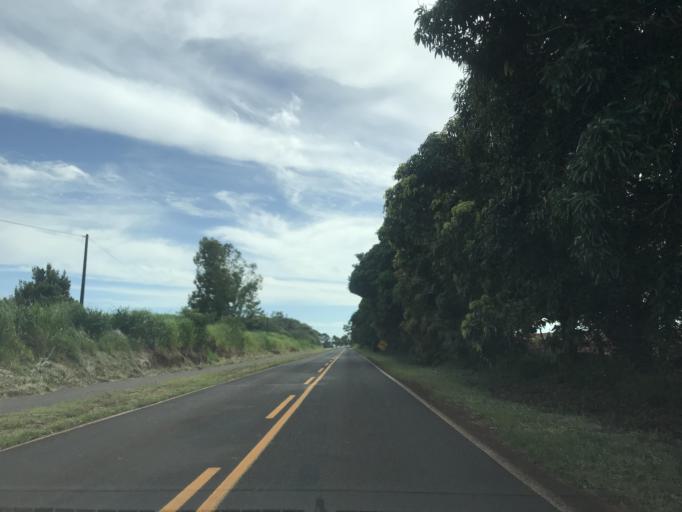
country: BR
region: Parana
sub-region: Terra Rica
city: Terra Rica
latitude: -22.7554
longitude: -52.6287
